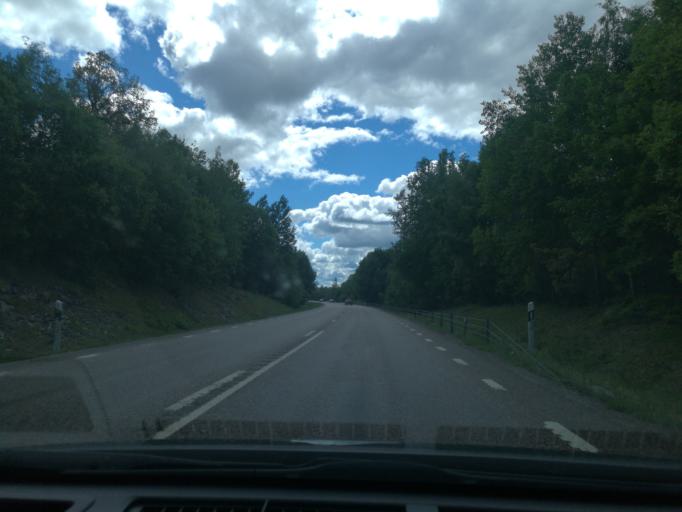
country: SE
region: Soedermanland
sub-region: Eskilstuna Kommun
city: Kvicksund
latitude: 59.4774
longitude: 16.3050
